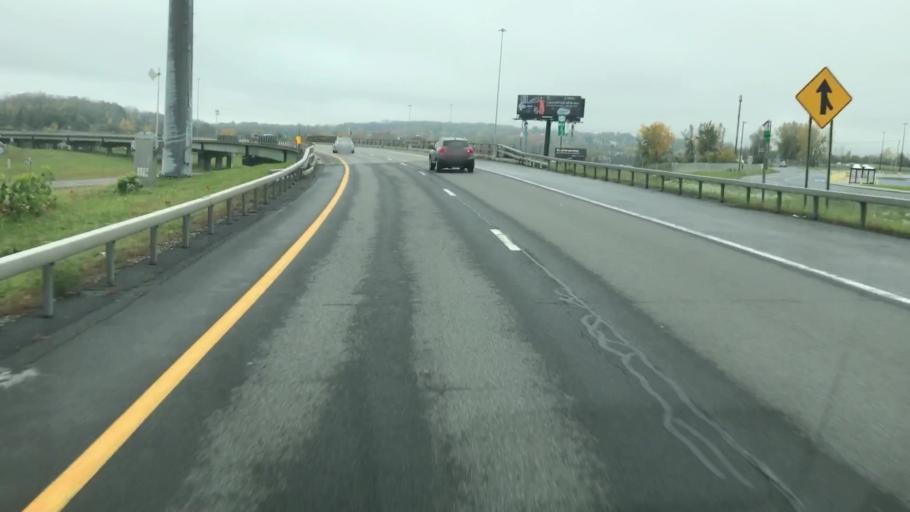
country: US
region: New York
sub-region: Onondaga County
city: Lakeland
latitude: 43.0807
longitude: -76.2188
